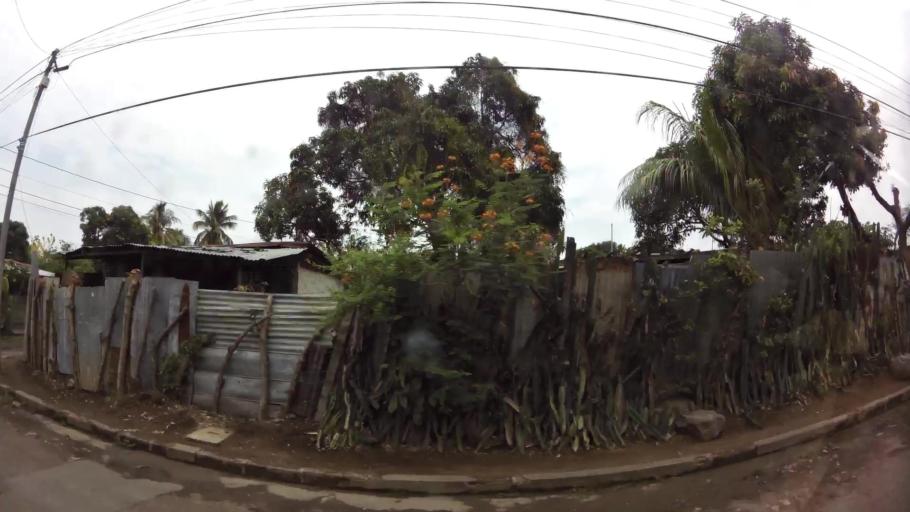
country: NI
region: Granada
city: Granada
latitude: 11.9187
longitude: -85.9666
